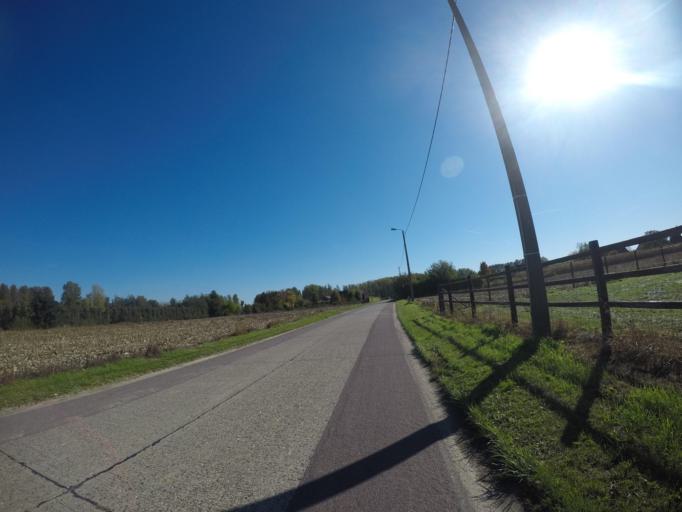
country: BE
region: Flanders
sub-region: Provincie Limburg
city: Alken
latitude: 50.8601
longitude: 5.3198
